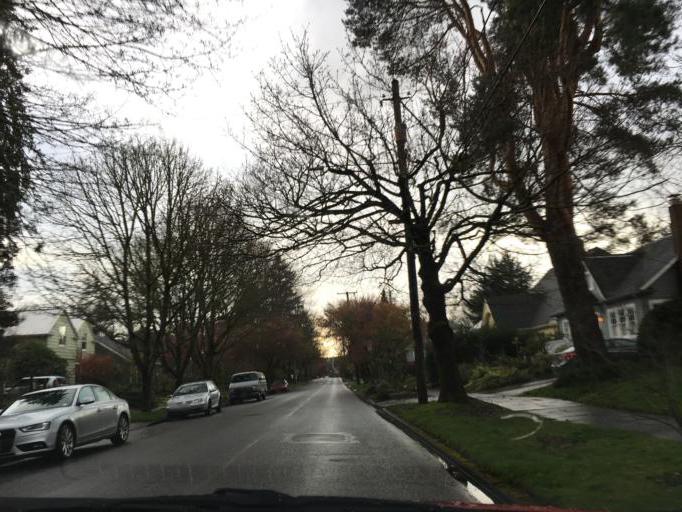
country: US
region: Oregon
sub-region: Multnomah County
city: Portland
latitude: 45.5421
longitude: -122.6262
